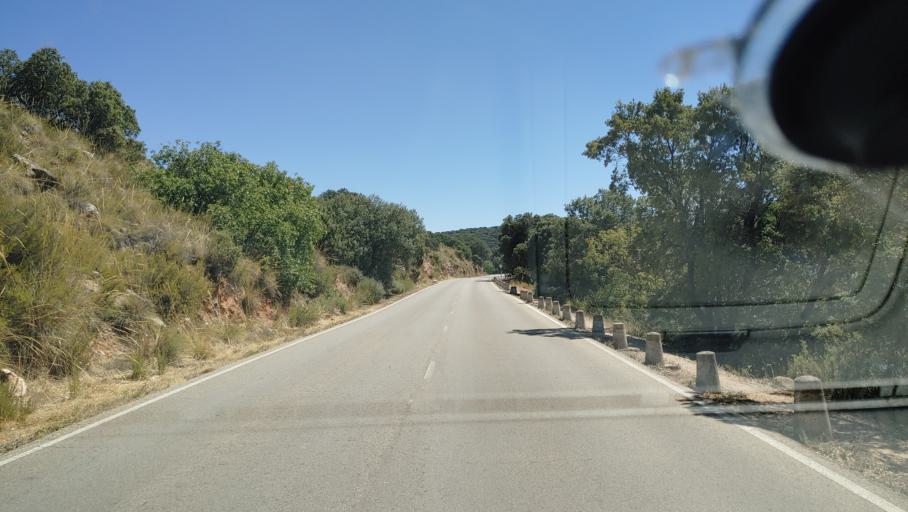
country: ES
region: Castille-La Mancha
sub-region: Provincia de Ciudad Real
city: Ruidera
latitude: 38.9597
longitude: -2.8700
